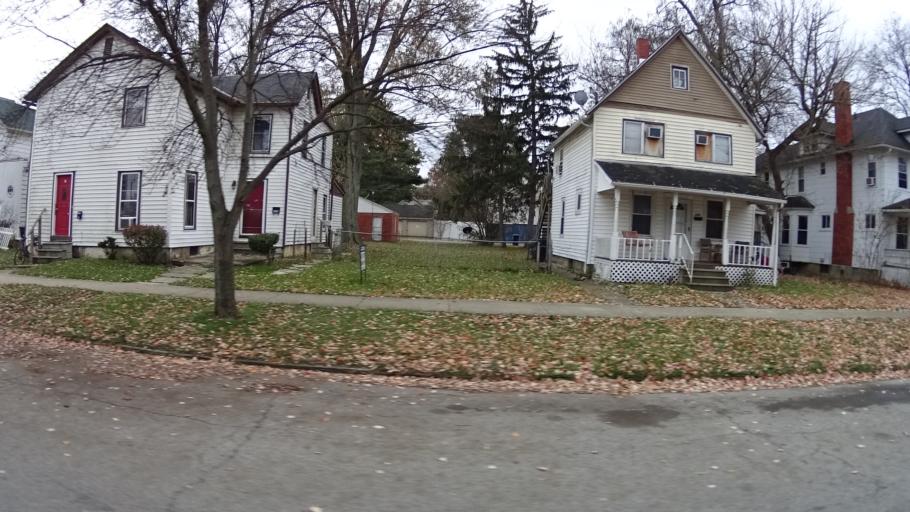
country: US
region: Ohio
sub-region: Lorain County
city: Elyria
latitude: 41.3630
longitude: -82.1057
